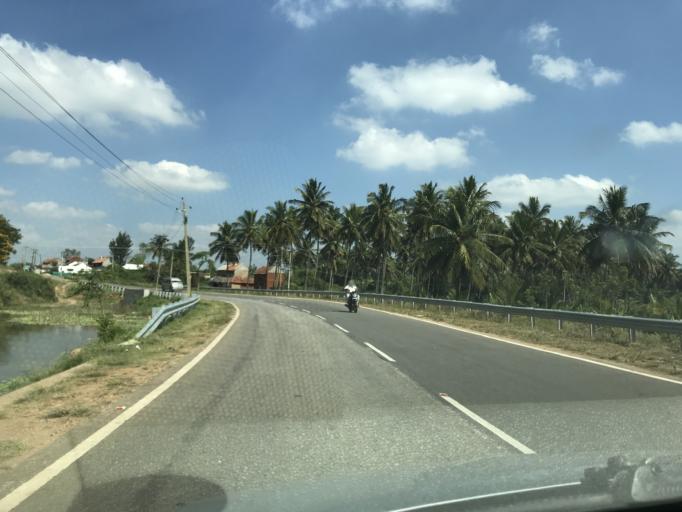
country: IN
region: Karnataka
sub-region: Mysore
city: Heggadadevankote
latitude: 12.1681
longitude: 76.2795
